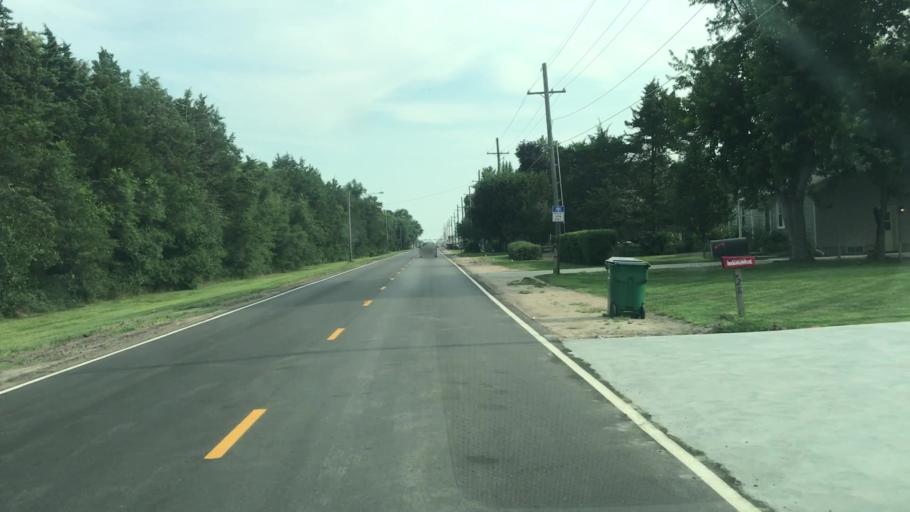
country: US
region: Nebraska
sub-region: Hall County
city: Grand Island
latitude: 40.9509
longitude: -98.3788
